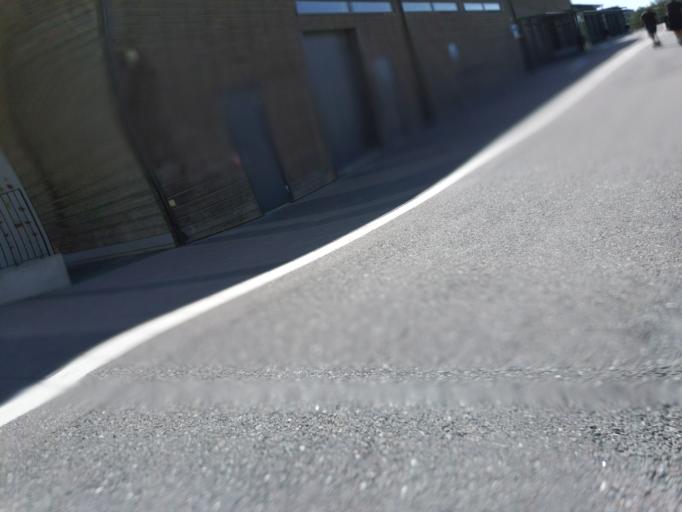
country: SE
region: Stockholm
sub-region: Solna Kommun
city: Rasunda
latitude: 59.3821
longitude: 17.9723
